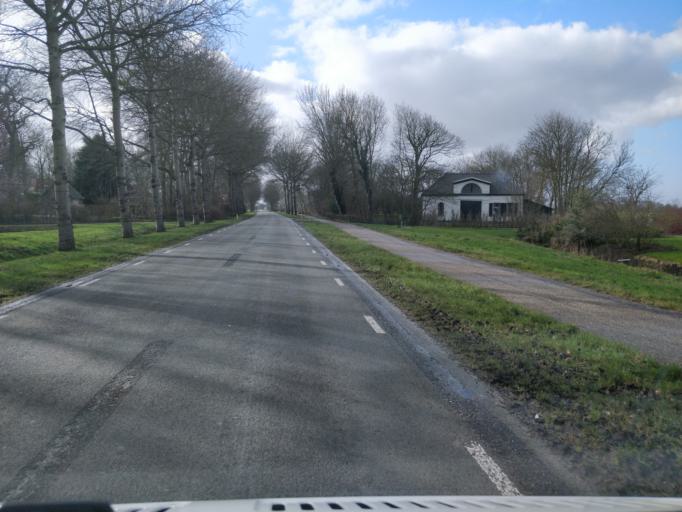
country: NL
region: Friesland
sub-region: Gemeente Franekeradeel
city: Sexbierum
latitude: 53.2174
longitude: 5.4769
